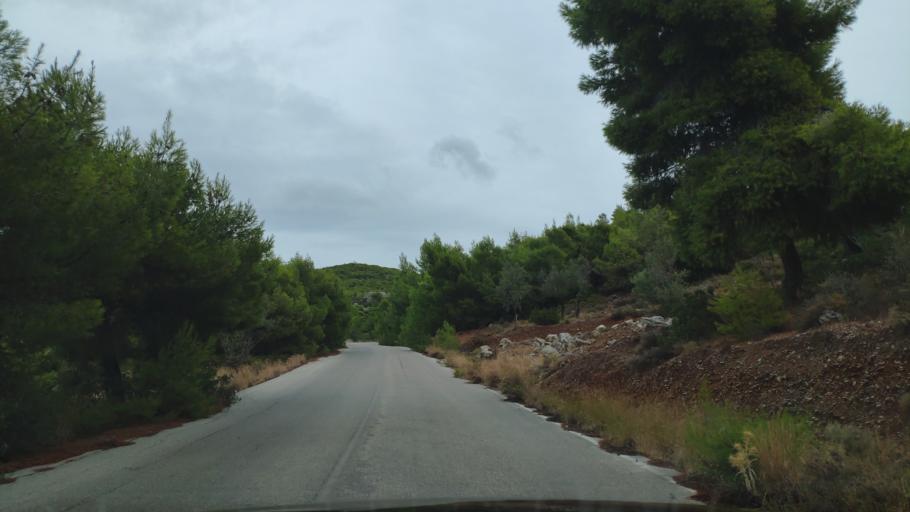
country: GR
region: Peloponnese
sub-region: Nomos Korinthias
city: Perachora
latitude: 38.0050
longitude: 22.9327
